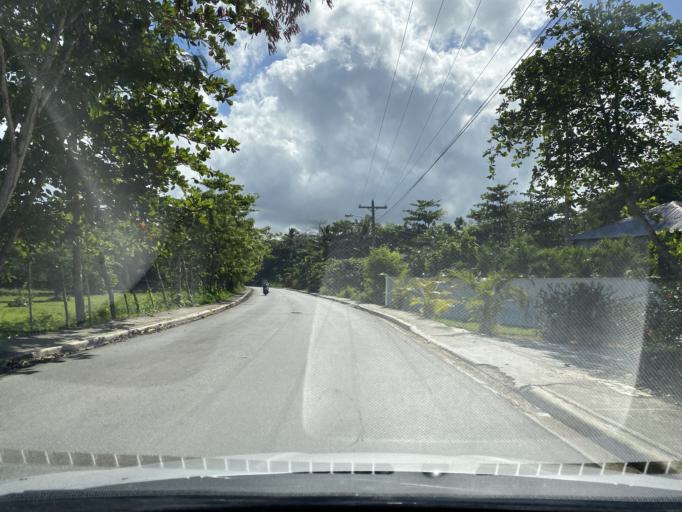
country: DO
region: Samana
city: Las Terrenas
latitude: 19.3233
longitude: -69.5292
